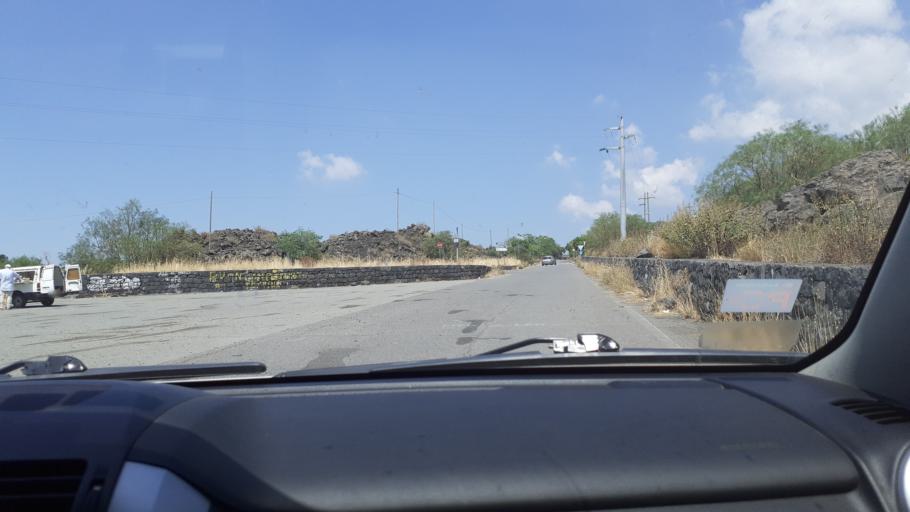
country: IT
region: Sicily
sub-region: Catania
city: Nicolosi
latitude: 37.6453
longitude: 14.9952
